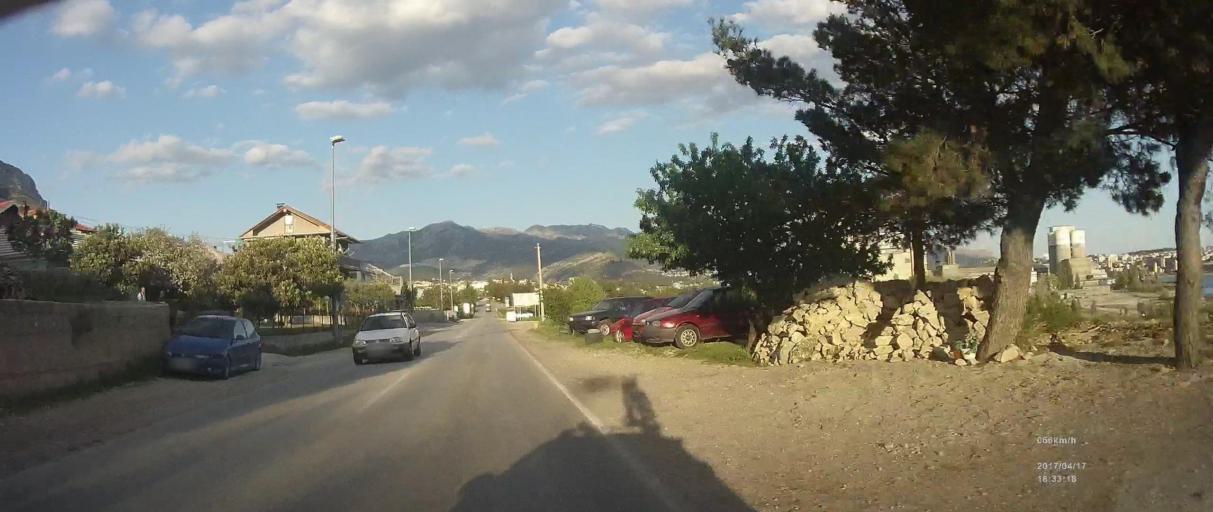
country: HR
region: Splitsko-Dalmatinska
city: Vranjic
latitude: 43.5411
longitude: 16.4576
